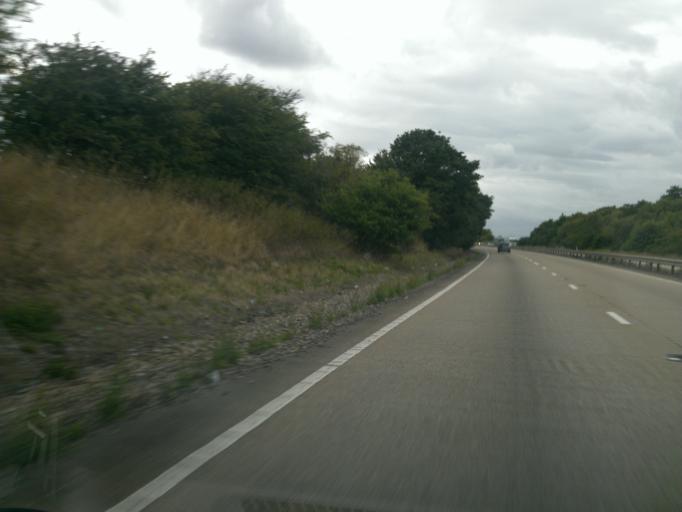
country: GB
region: England
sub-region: Essex
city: Alresford
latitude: 51.8936
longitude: 1.0082
